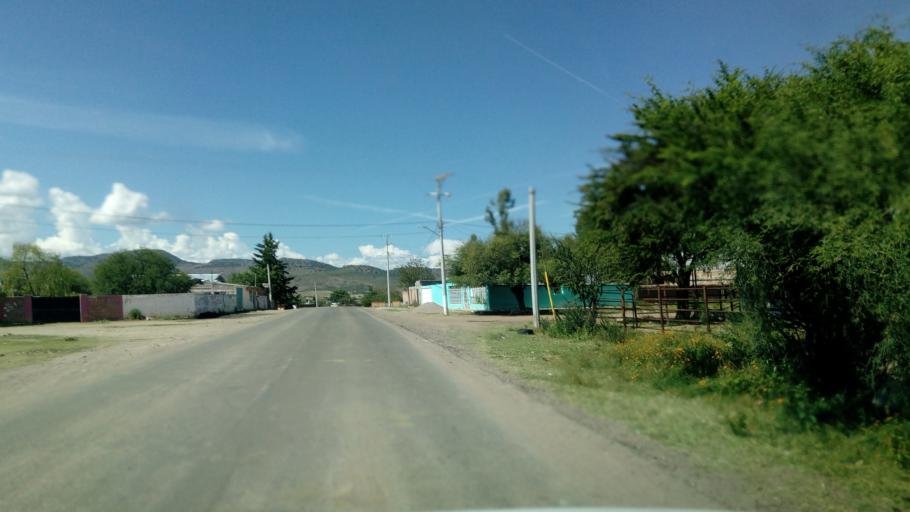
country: MX
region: Durango
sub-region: Durango
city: Jose Refugio Salcido
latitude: 23.8493
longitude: -104.4761
